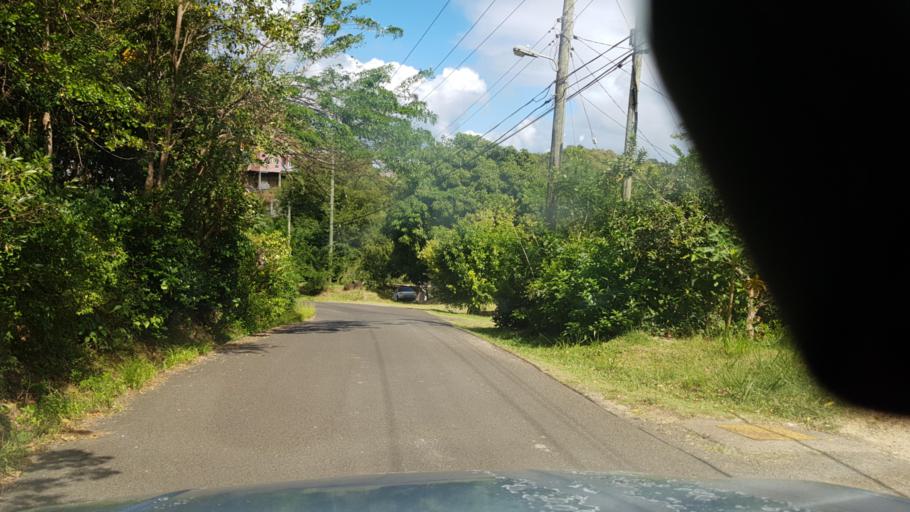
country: LC
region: Gros-Islet
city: Gros Islet
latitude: 14.0543
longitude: -60.9499
